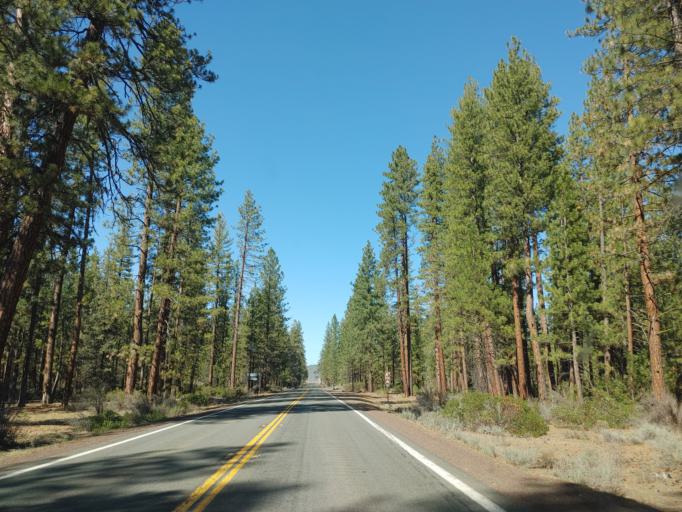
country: US
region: California
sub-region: Shasta County
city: Burney
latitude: 40.6829
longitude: -121.4236
